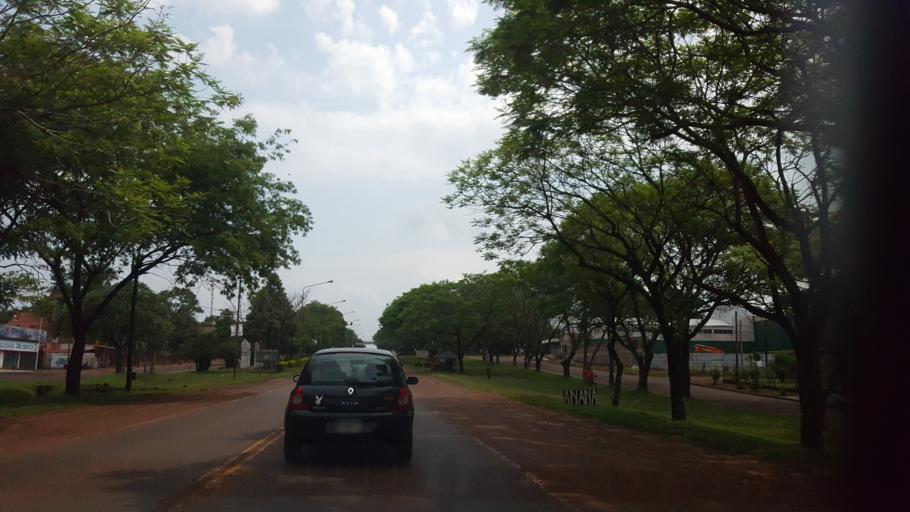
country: AR
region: Misiones
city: Jardin America
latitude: -27.0443
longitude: -55.2372
